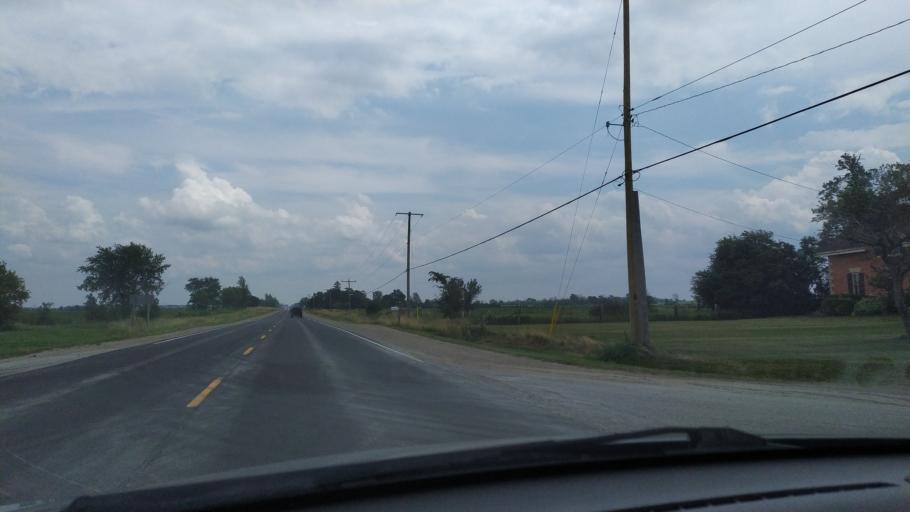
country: CA
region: Ontario
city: Stratford
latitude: 43.3700
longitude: -80.8875
